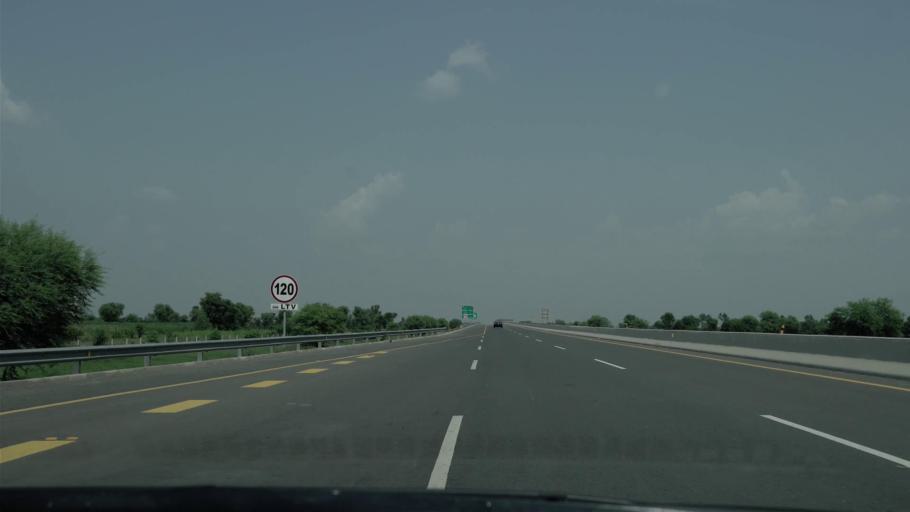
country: PK
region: Punjab
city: Gojra
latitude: 31.1868
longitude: 72.6447
